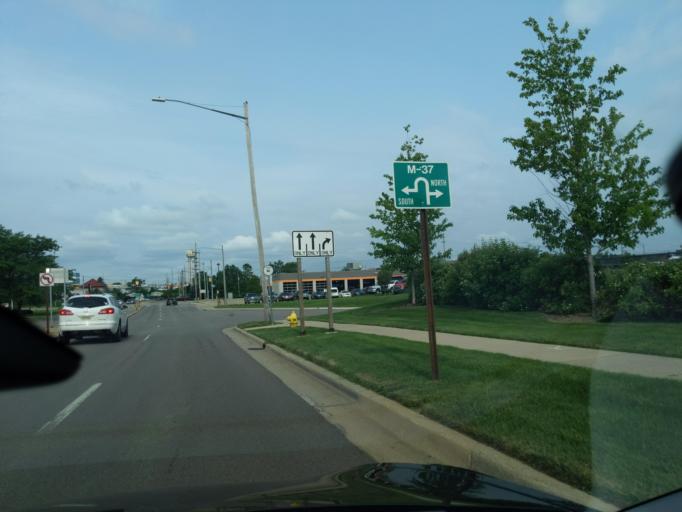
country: US
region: Michigan
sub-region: Kent County
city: East Grand Rapids
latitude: 42.9092
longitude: -85.5811
